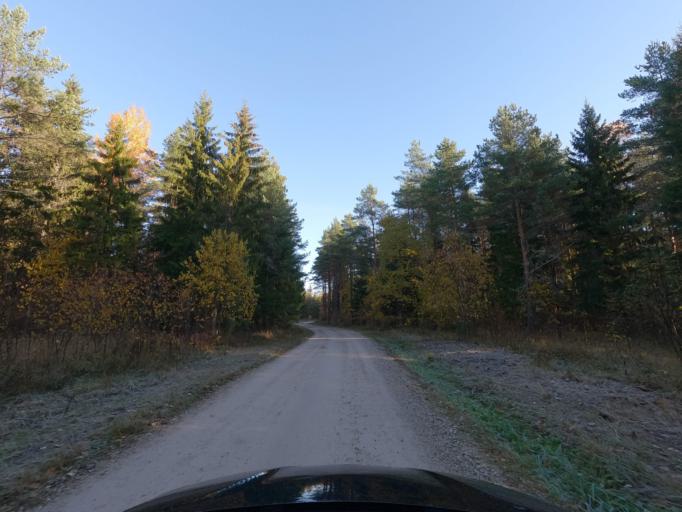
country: EE
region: Raplamaa
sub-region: Kohila vald
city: Kohila
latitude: 59.1217
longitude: 24.7645
